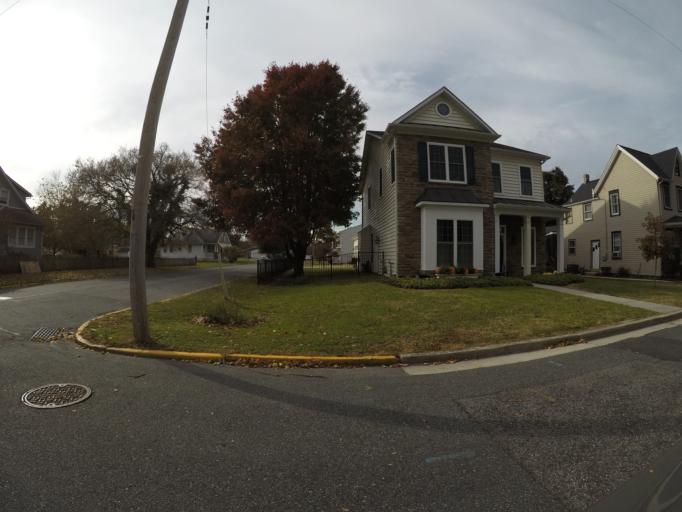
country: US
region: Maryland
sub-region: Harford County
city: Havre de Grace
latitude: 39.5407
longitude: -76.0896
